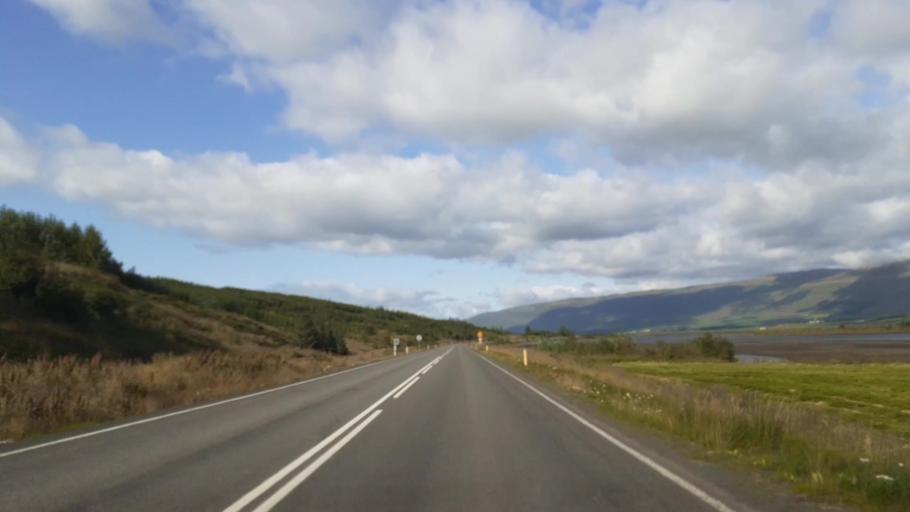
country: IS
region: Northeast
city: Akureyri
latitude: 65.5820
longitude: -18.0903
